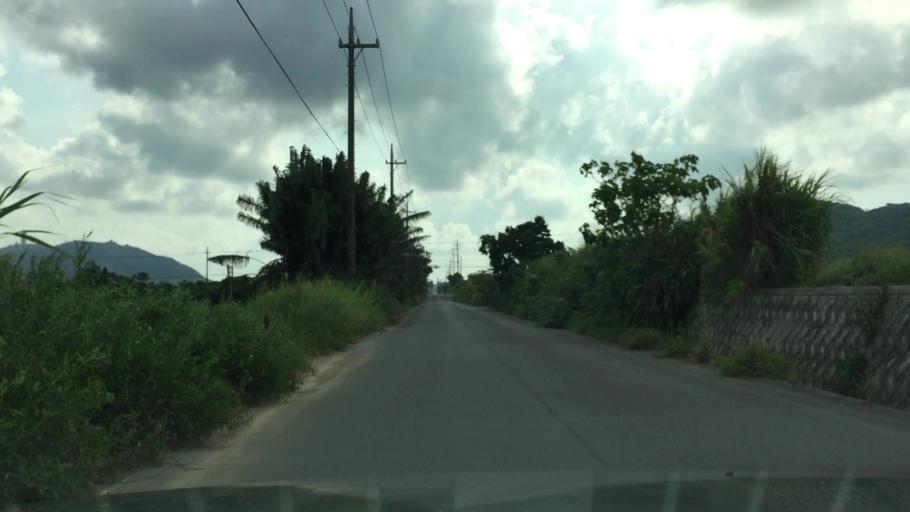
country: JP
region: Okinawa
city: Ishigaki
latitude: 24.3981
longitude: 124.1968
